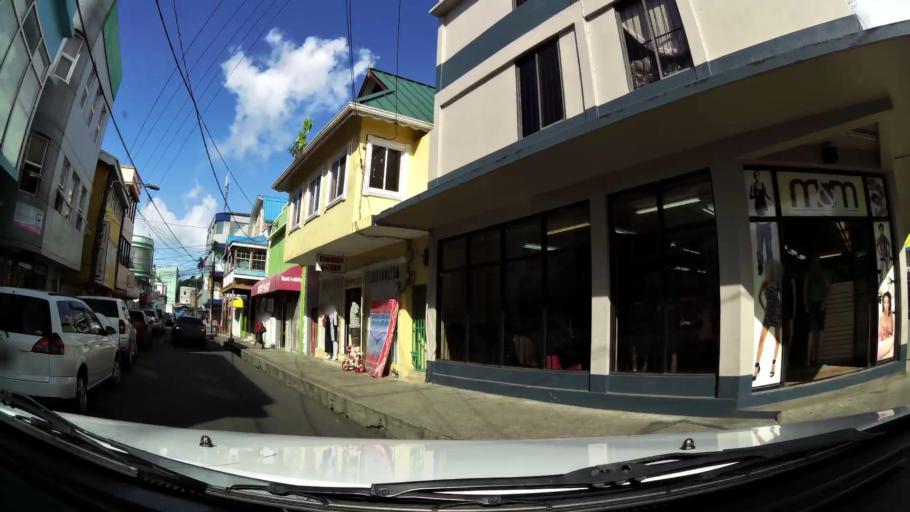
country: LC
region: Castries Quarter
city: Bisee
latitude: 14.0096
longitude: -60.9878
